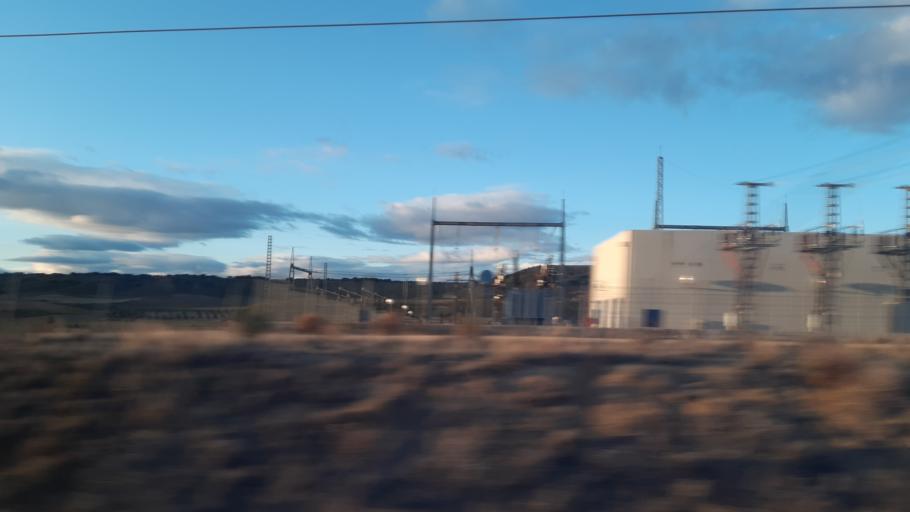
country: ES
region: Madrid
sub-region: Provincia de Madrid
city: Anchuelo
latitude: 40.4632
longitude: -3.2960
